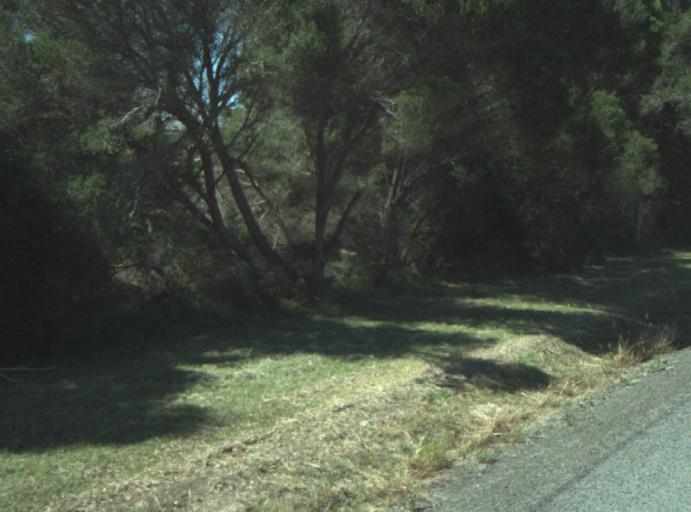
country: AU
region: Victoria
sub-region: Greater Geelong
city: Breakwater
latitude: -38.2038
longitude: 144.3615
